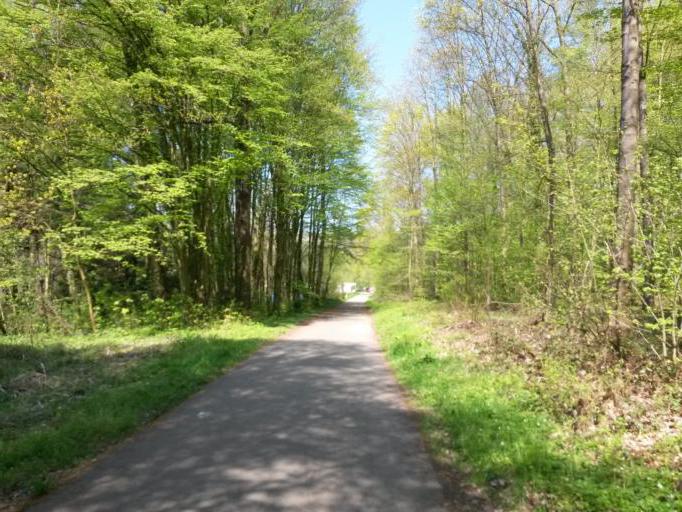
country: DE
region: Baden-Wuerttemberg
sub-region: Karlsruhe Region
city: Konigsbach-Stein
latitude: 48.9756
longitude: 8.5519
